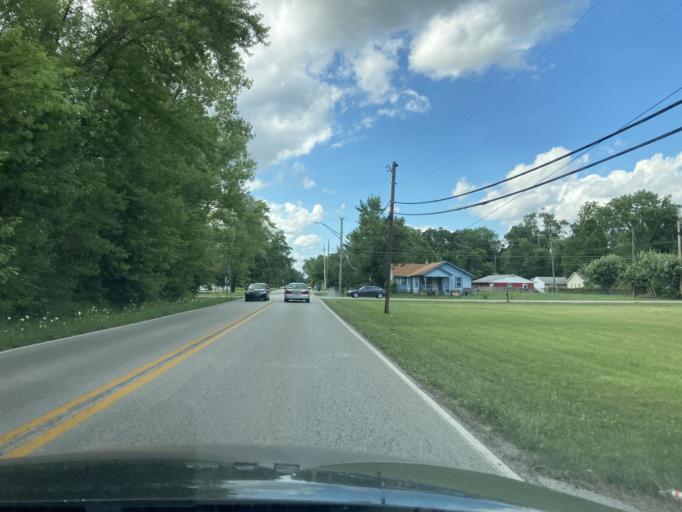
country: US
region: Indiana
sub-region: Marion County
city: Meridian Hills
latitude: 39.8632
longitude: -86.2121
